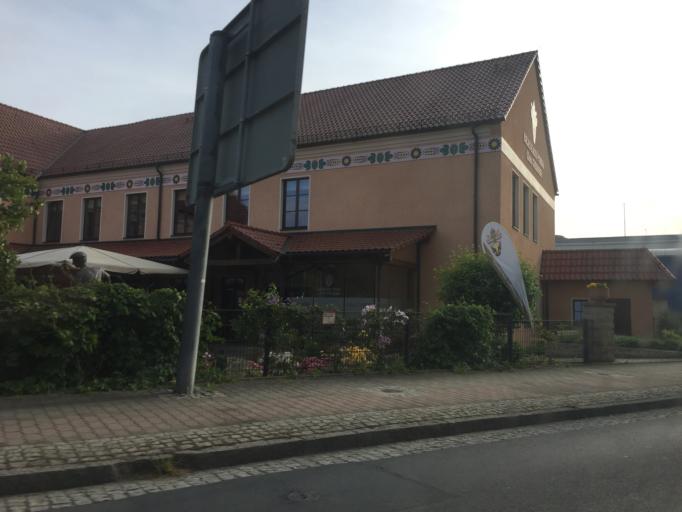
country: DE
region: Saxony
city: Pirna
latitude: 50.9802
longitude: 13.9433
